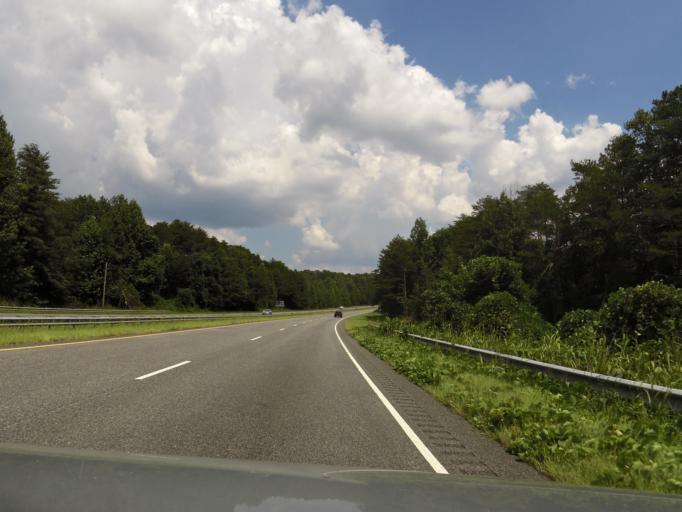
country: US
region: North Carolina
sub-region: Polk County
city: Columbus
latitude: 35.2667
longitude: -82.1701
